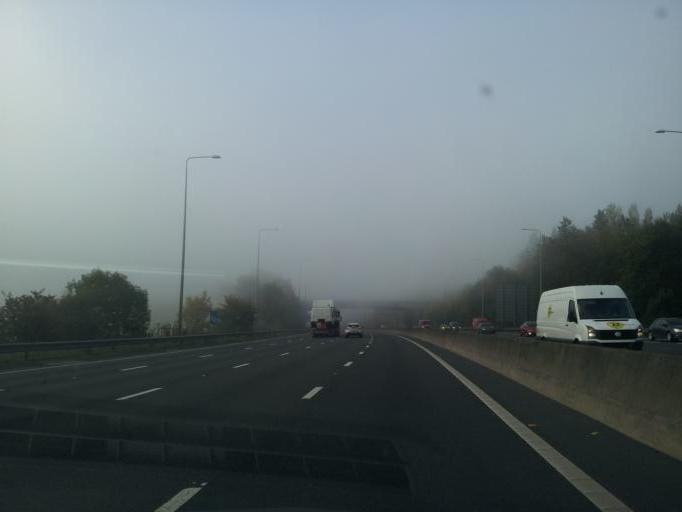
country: GB
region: England
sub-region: Kirklees
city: Cleckheaton
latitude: 53.7207
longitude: -1.7427
